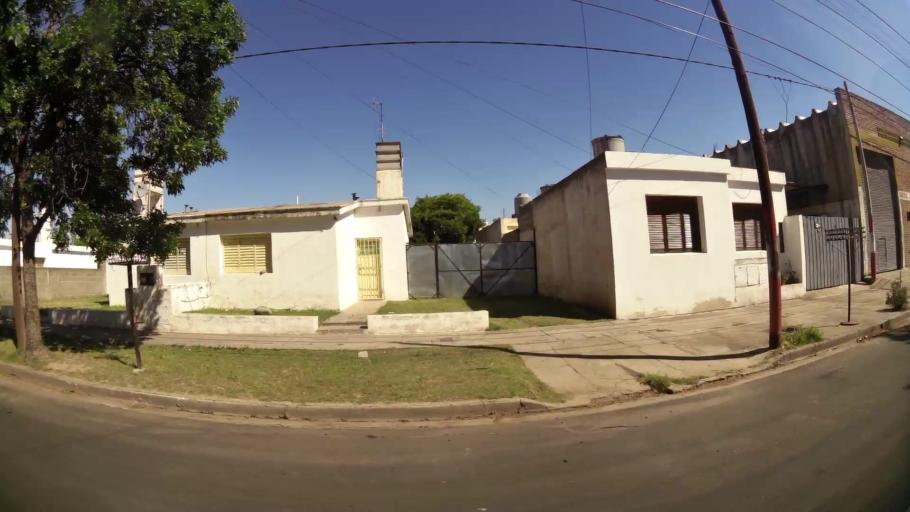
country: AR
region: Cordoba
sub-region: Departamento de Capital
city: Cordoba
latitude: -31.3716
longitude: -64.1682
